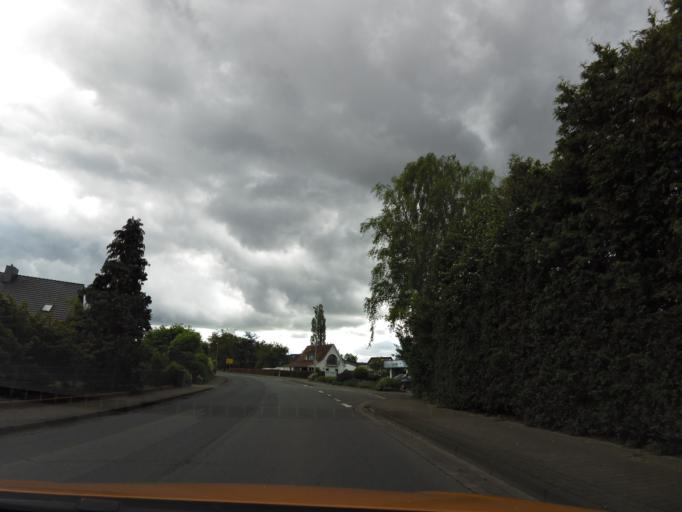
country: DE
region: Lower Saxony
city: Delmenhorst
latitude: 53.0898
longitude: 8.5817
